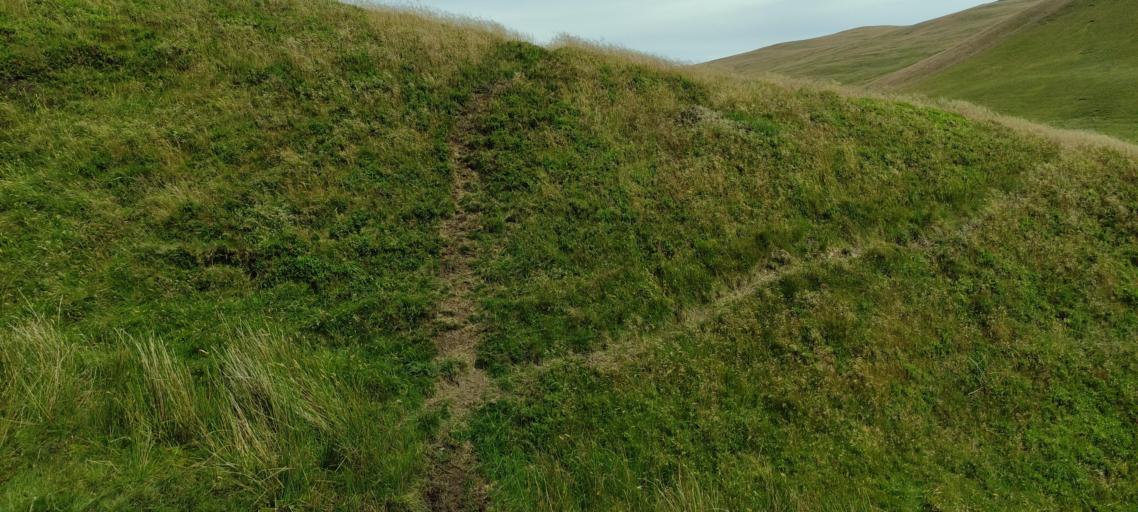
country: GB
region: England
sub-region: Cumbria
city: Frizington
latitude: 54.5503
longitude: -3.3890
